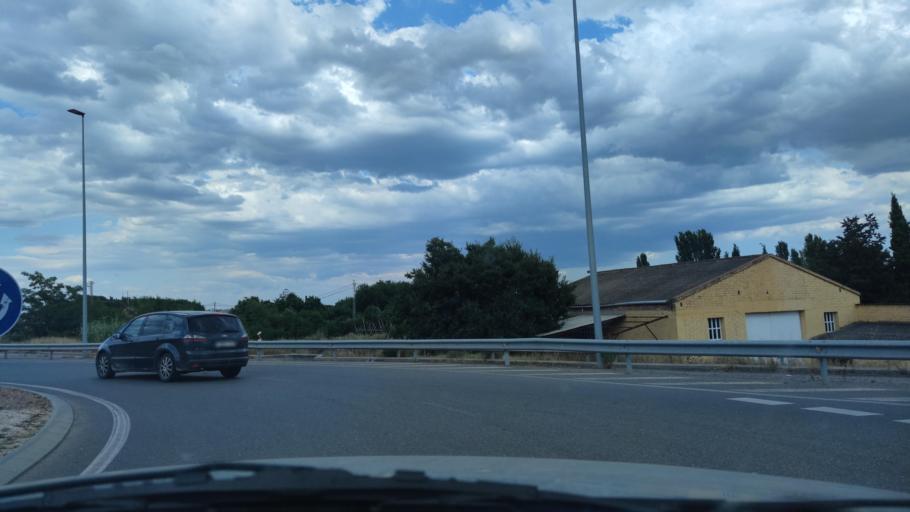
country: ES
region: Catalonia
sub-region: Provincia de Lleida
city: Lleida
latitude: 41.5993
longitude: 0.5983
